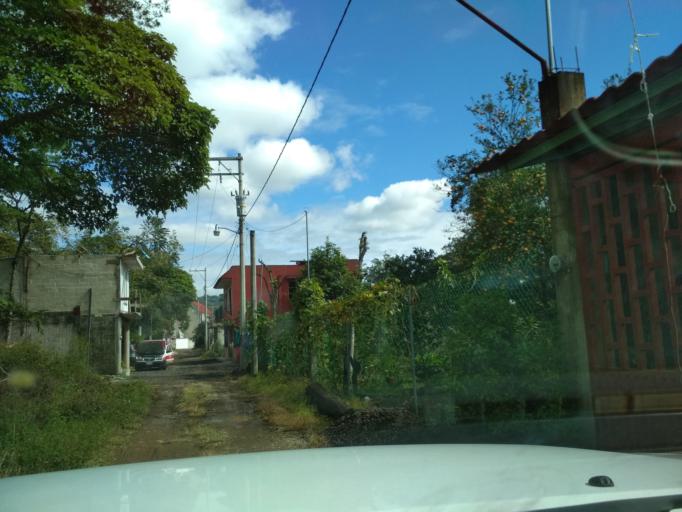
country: MX
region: Veracruz
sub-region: Coatepec
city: Las Lomas
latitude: 19.4364
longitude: -96.9227
